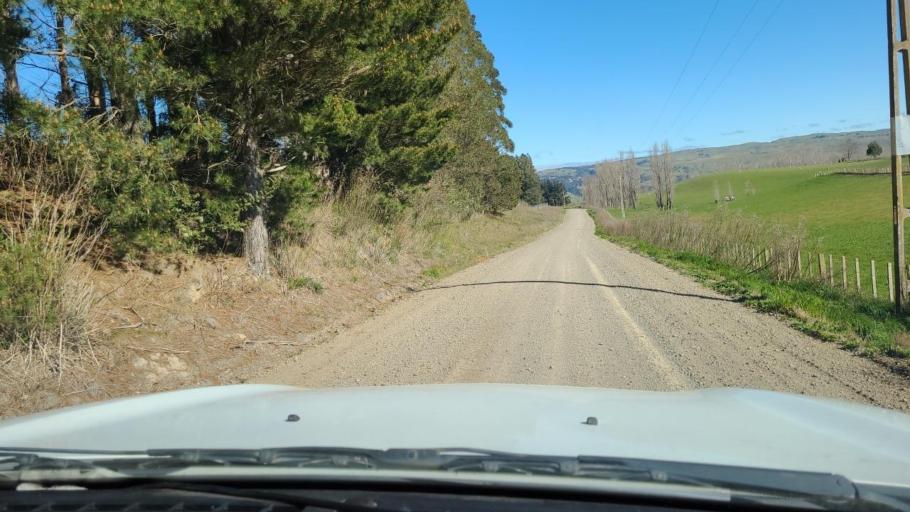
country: NZ
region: Hawke's Bay
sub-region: Napier City
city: Taradale
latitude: -39.4936
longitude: 176.4892
